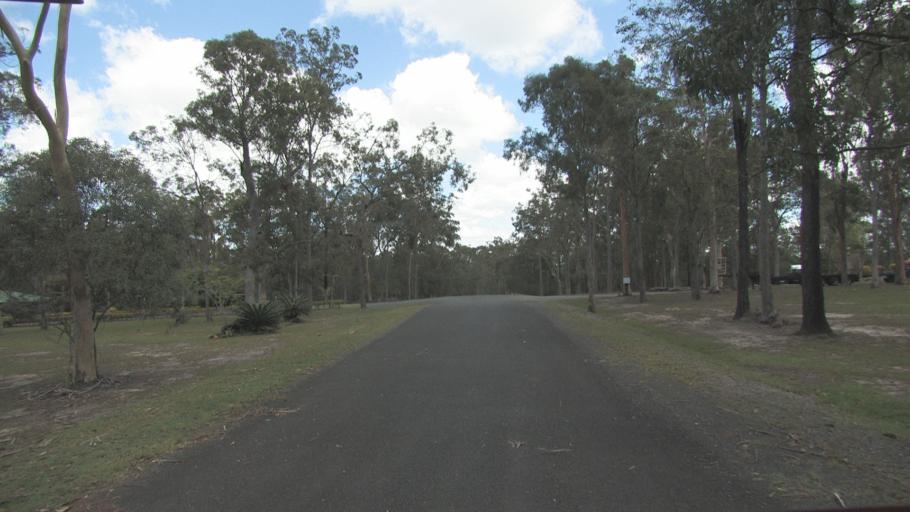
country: AU
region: Queensland
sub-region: Redland
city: Redland Bay
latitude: -27.6502
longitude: 153.2434
